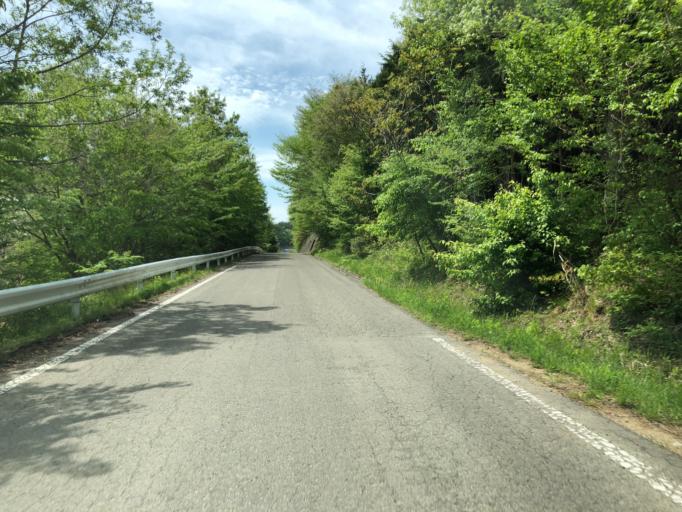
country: JP
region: Fukushima
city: Yanagawamachi-saiwaicho
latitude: 37.7199
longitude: 140.7075
